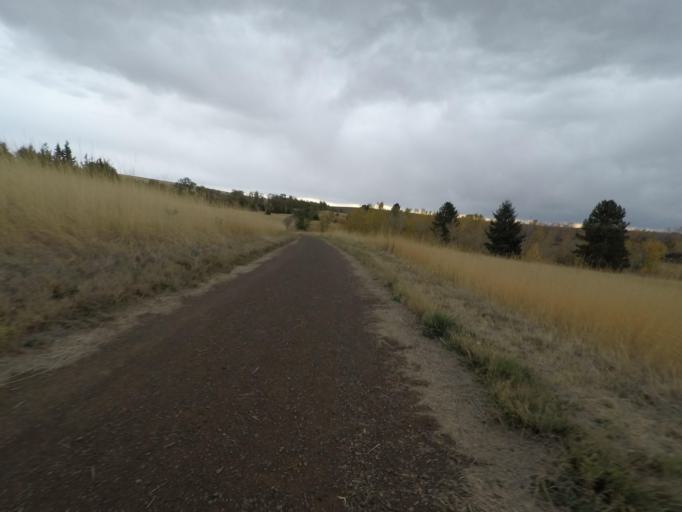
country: US
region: Washington
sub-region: Walla Walla County
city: Walla Walla East
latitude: 46.0662
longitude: -118.2566
